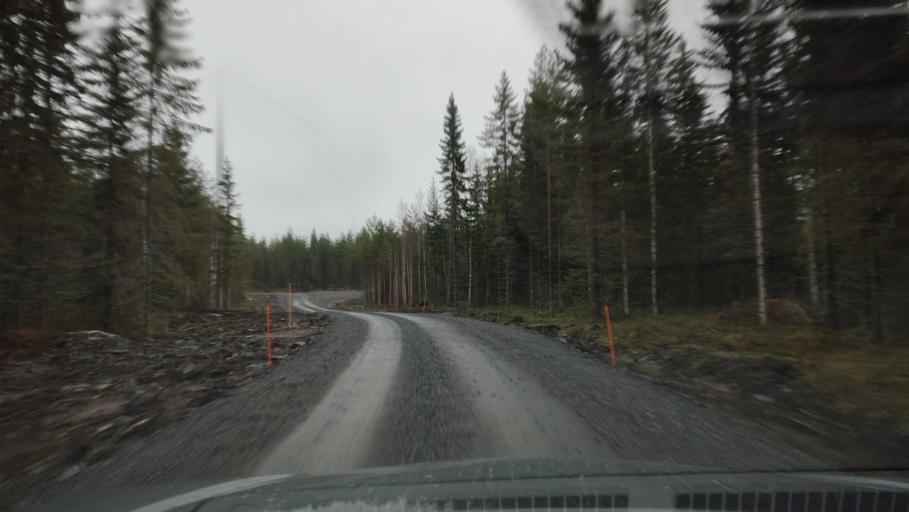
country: FI
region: Southern Ostrobothnia
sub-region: Suupohja
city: Karijoki
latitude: 62.1633
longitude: 21.5876
